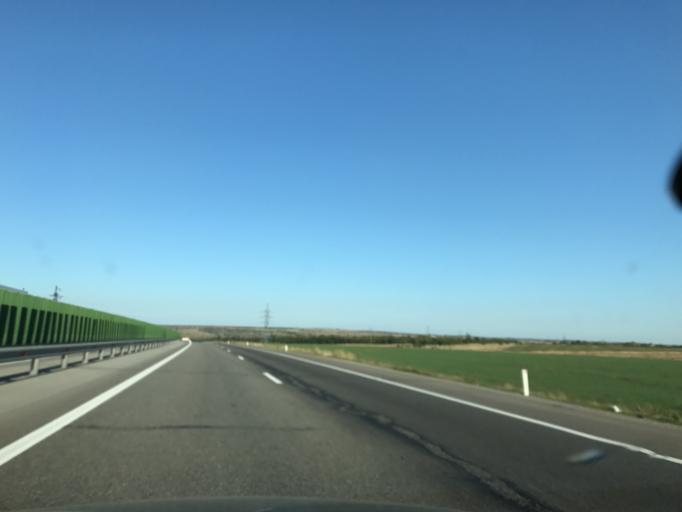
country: RU
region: Rostov
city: Tarasovskiy
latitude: 48.7450
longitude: 40.3906
